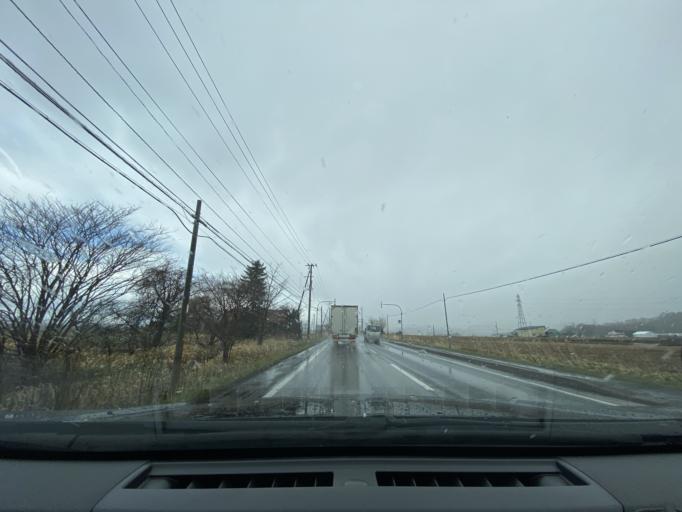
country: JP
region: Hokkaido
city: Fukagawa
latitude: 43.6633
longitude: 141.9978
